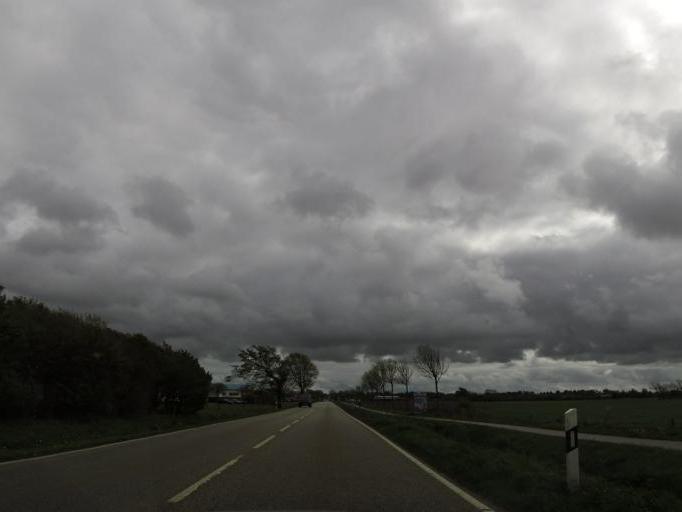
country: DE
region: Schleswig-Holstein
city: Suderlugum
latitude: 54.8818
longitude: 8.9087
